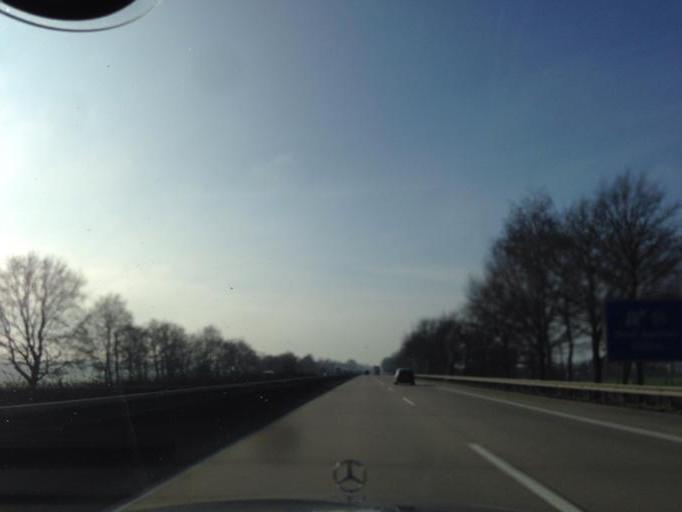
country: DE
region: Lower Saxony
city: Gross Ippener
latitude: 52.9806
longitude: 8.6319
